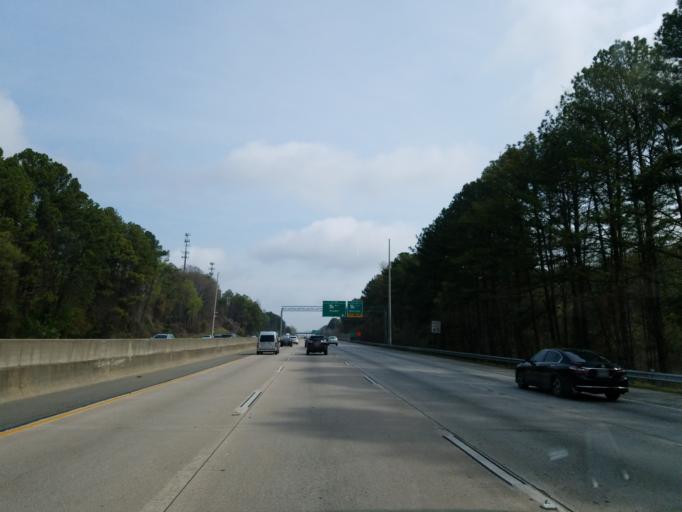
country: US
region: Georgia
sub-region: Fulton County
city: Roswell
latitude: 34.0121
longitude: -84.3311
